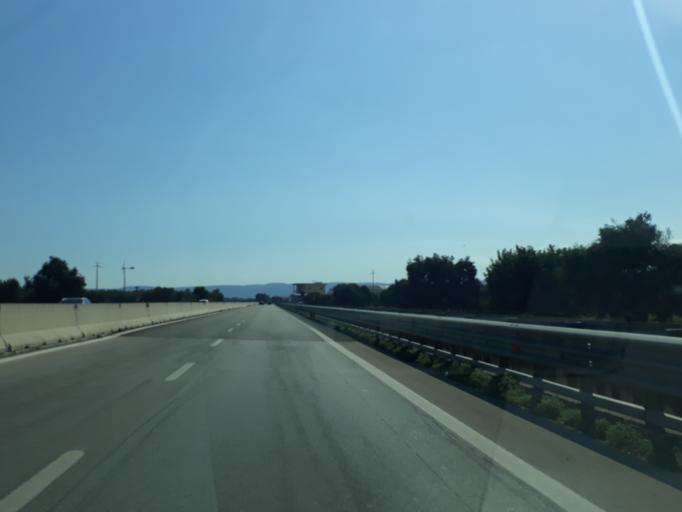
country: IT
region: Apulia
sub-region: Provincia di Brindisi
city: Fasano
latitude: 40.8632
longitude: 17.3471
